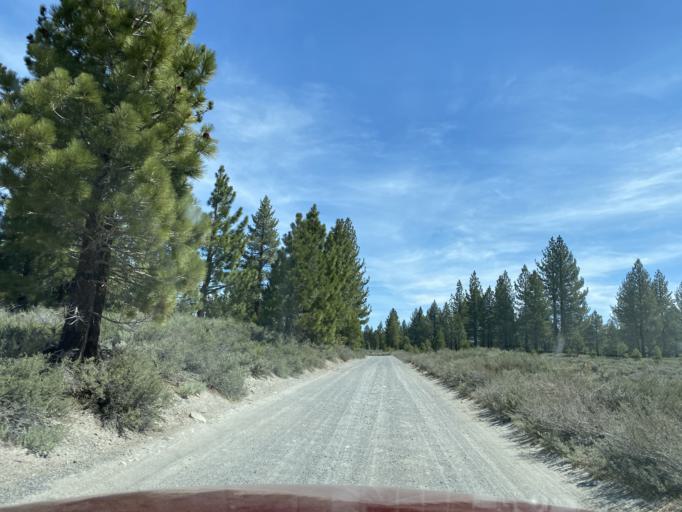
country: US
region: California
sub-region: Mono County
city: Mammoth Lakes
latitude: 37.7712
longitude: -119.0176
